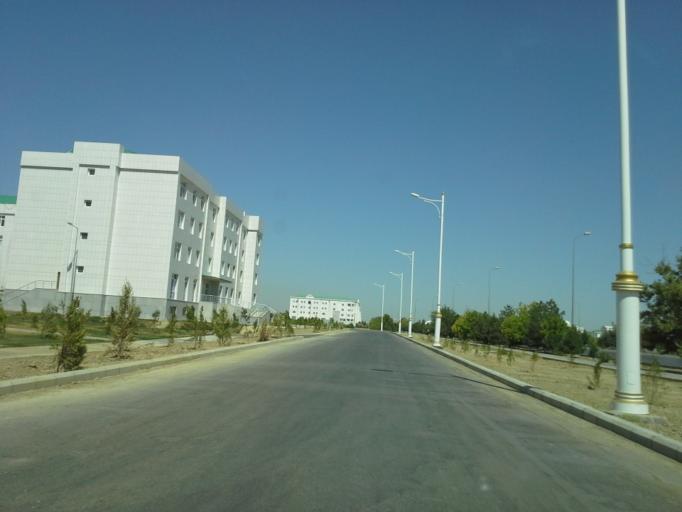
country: TM
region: Ahal
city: Ashgabat
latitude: 37.9836
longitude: 58.3310
